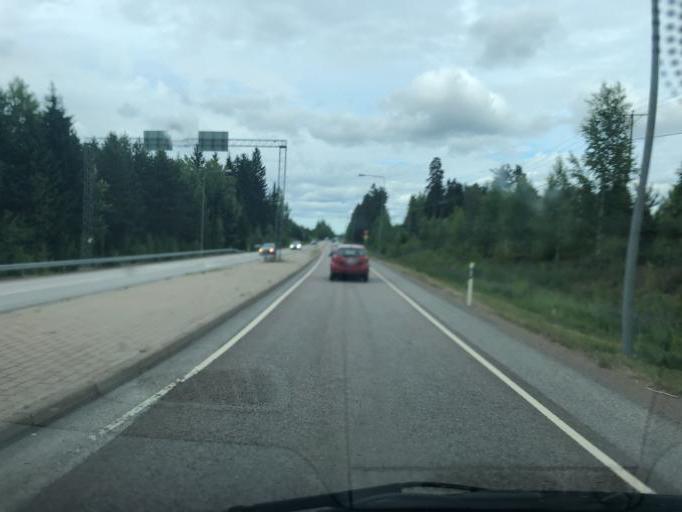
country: FI
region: Kymenlaakso
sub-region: Kouvola
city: Kouvola
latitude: 60.9126
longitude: 26.7685
